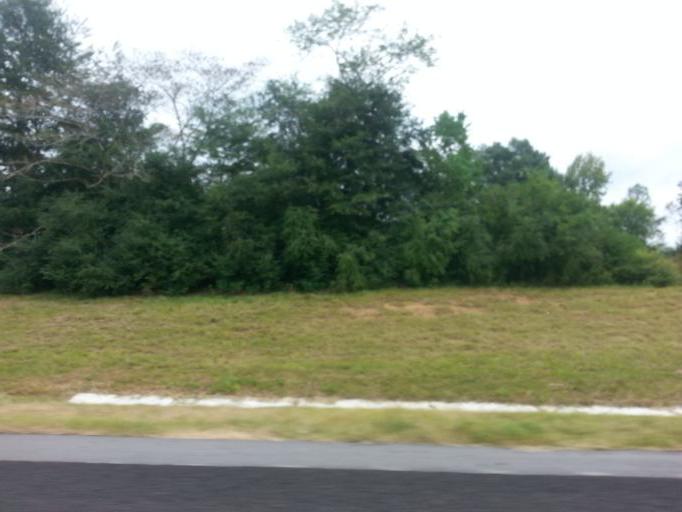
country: US
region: Alabama
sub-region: Conecuh County
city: Evergreen
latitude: 31.4168
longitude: -87.0079
